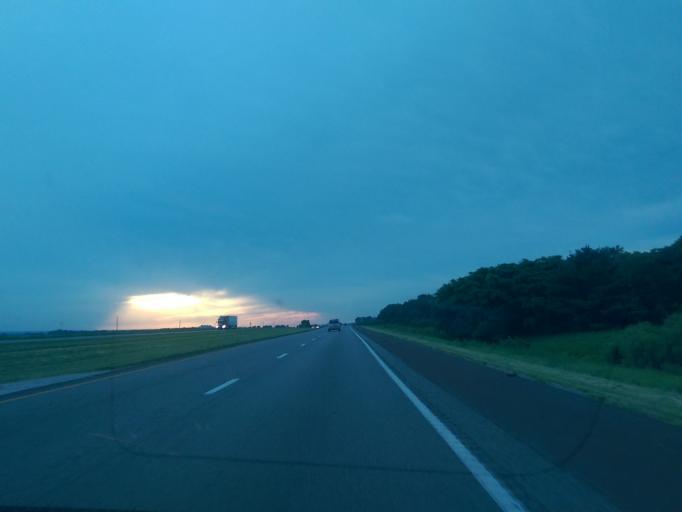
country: US
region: Missouri
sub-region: Holt County
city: Mound City
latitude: 40.1603
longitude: -95.2782
